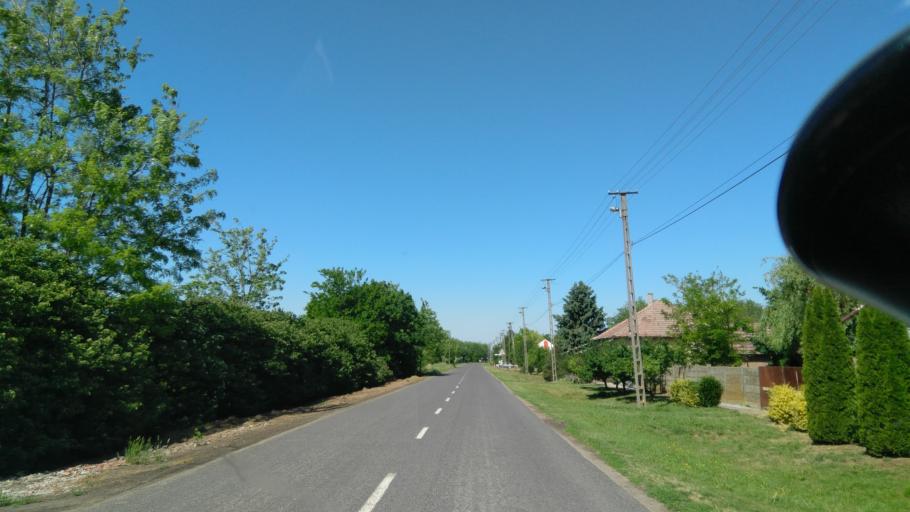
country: HU
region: Bekes
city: Kevermes
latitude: 46.4229
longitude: 21.1182
